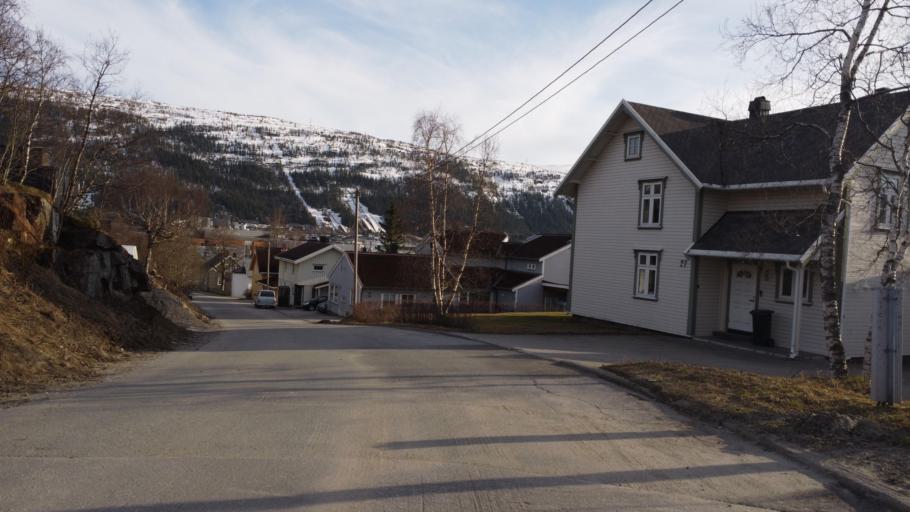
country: NO
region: Nordland
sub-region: Rana
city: Mo i Rana
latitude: 66.3146
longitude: 14.1350
